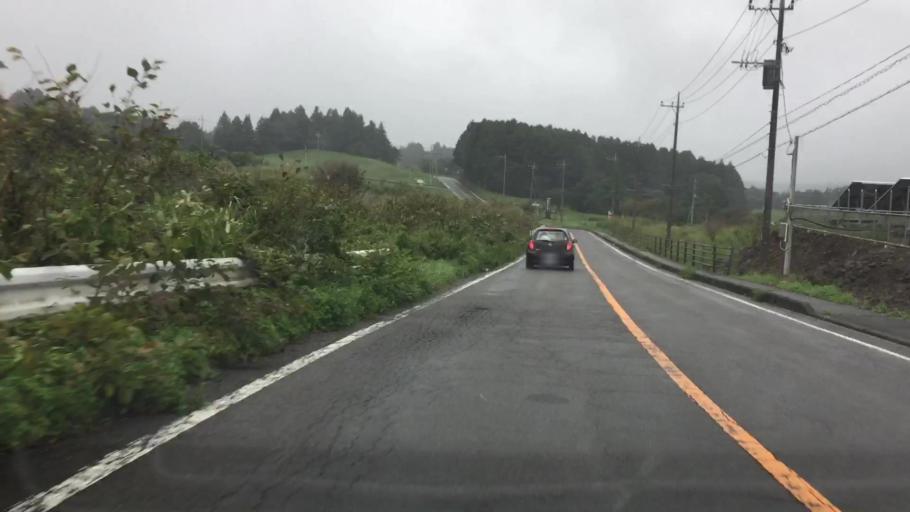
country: JP
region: Yamanashi
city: Fujikawaguchiko
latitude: 35.4038
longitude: 138.6138
